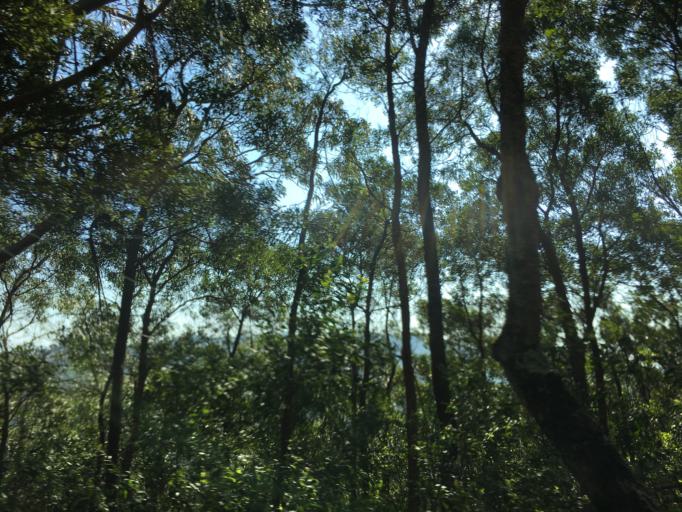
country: PT
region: Lisbon
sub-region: Sintra
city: Colares
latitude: 38.7730
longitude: -9.4360
